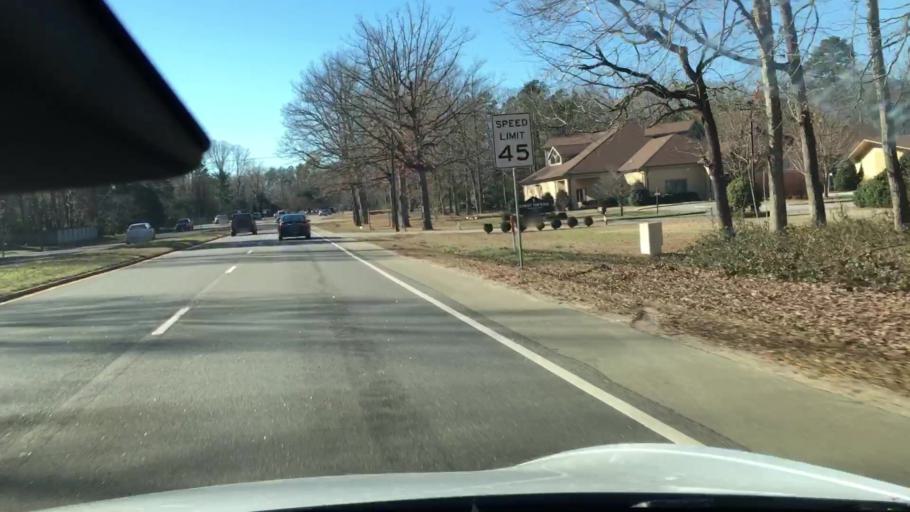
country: US
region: Virginia
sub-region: Chesterfield County
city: Bon Air
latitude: 37.5328
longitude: -77.5759
